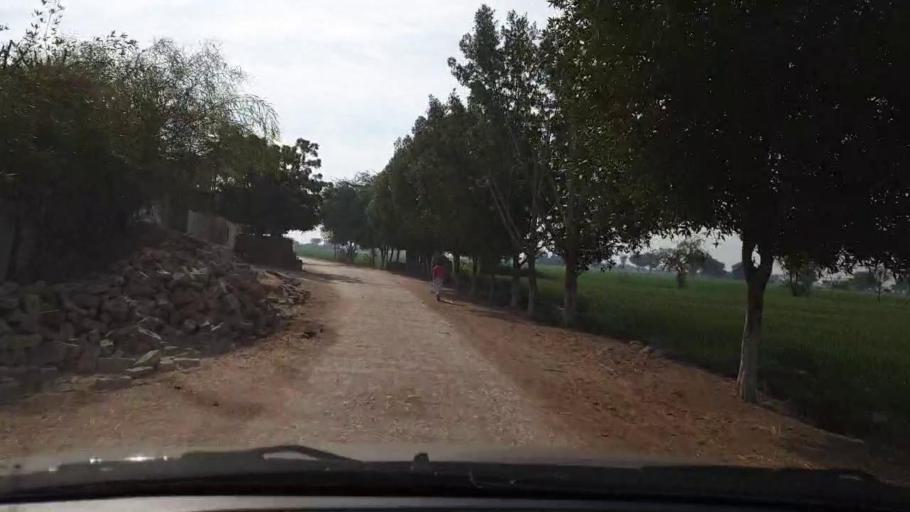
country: PK
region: Sindh
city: Shahpur Chakar
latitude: 26.1758
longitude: 68.6781
